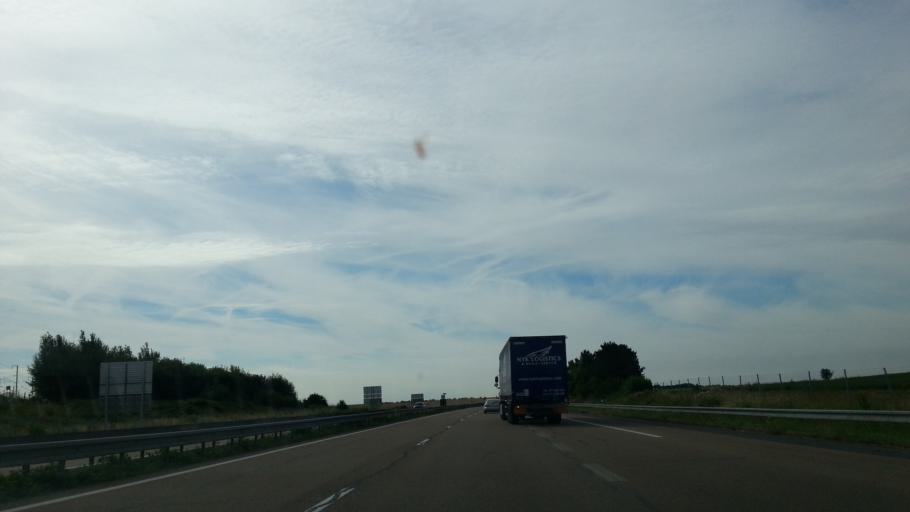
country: FR
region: Champagne-Ardenne
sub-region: Departement de la Marne
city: Verzy
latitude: 49.1129
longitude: 4.2510
